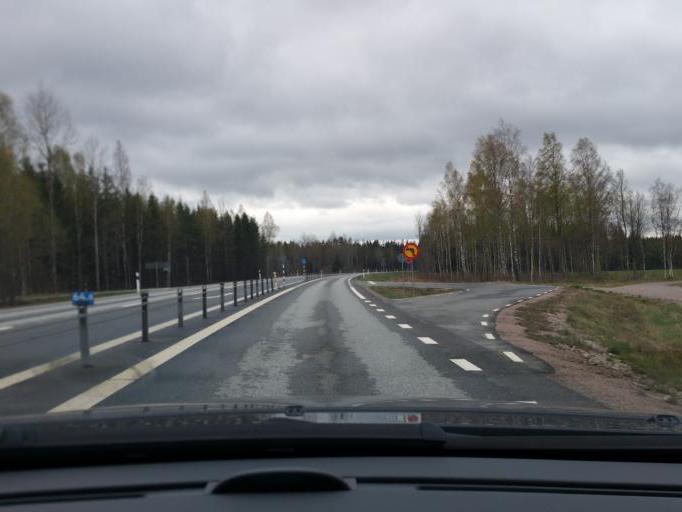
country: SE
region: Kronoberg
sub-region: Vaxjo Kommun
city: Vaexjoe
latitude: 56.9390
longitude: 14.7250
